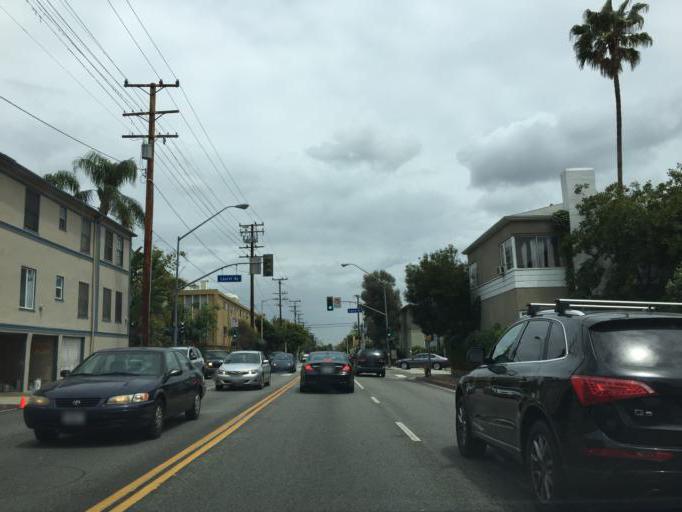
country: US
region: California
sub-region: Los Angeles County
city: West Hollywood
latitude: 34.0944
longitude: -118.3650
